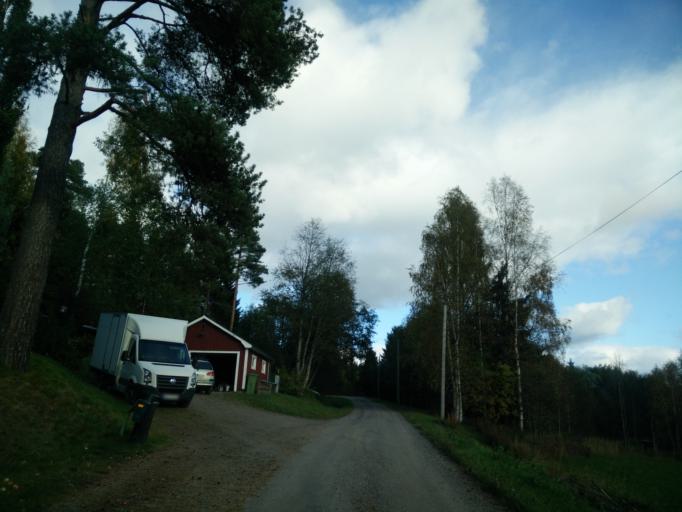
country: SE
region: Vaesternorrland
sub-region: Sundsvalls Kommun
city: Matfors
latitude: 62.3655
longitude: 17.0689
